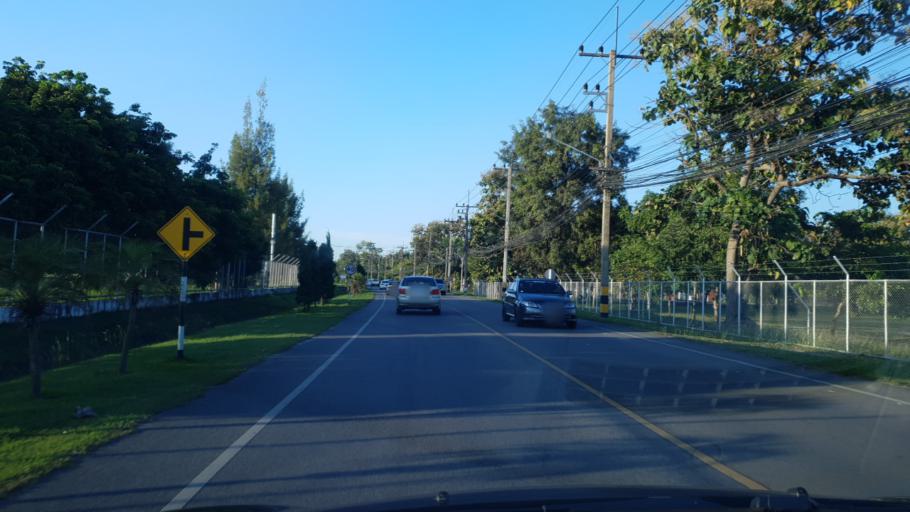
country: TH
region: Chiang Mai
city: Chiang Mai
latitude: 18.7767
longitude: 98.9671
